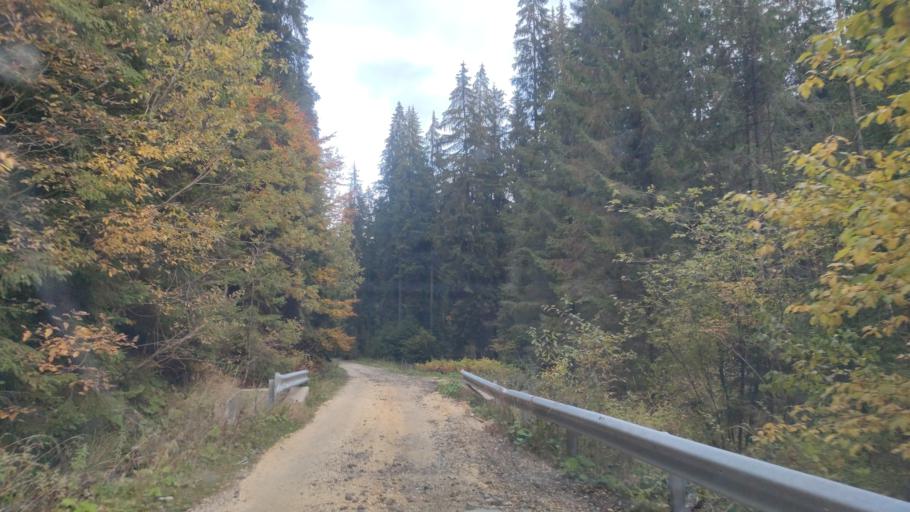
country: RO
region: Harghita
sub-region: Comuna Madaras
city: Madaras
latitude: 46.4706
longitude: 25.6302
